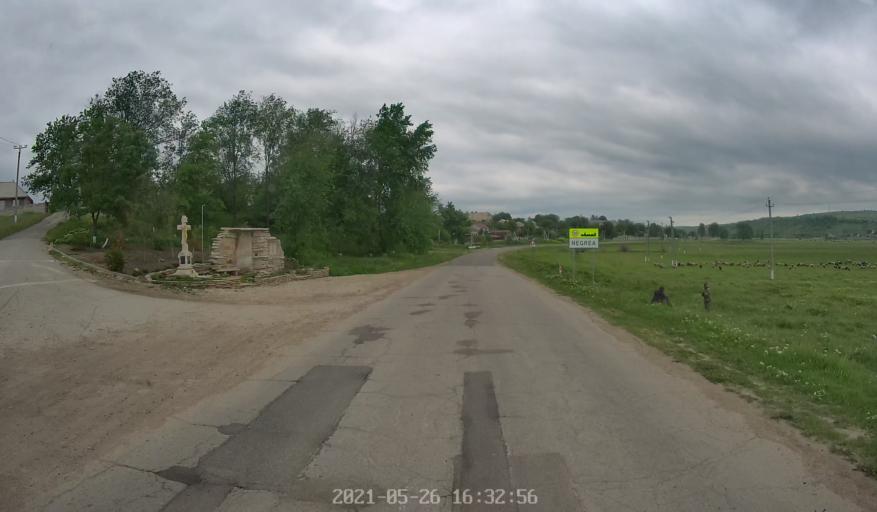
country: MD
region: Hincesti
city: Dancu
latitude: 46.8207
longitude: 28.3638
